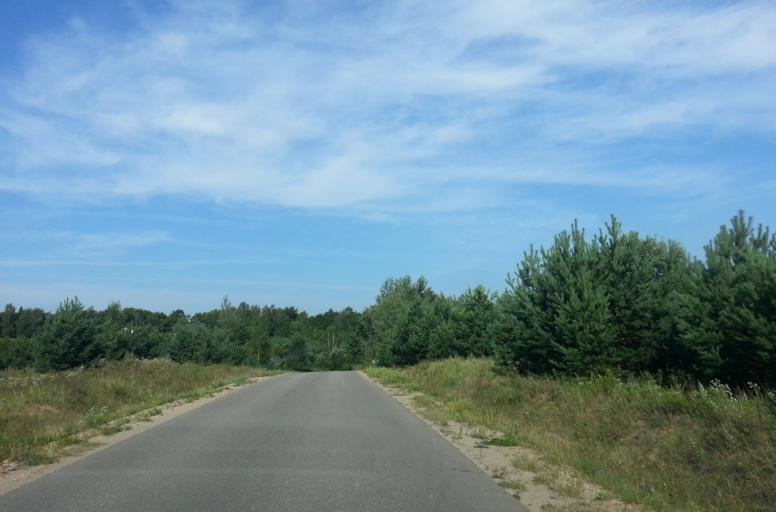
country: LT
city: Grigiskes
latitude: 54.7259
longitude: 25.0730
